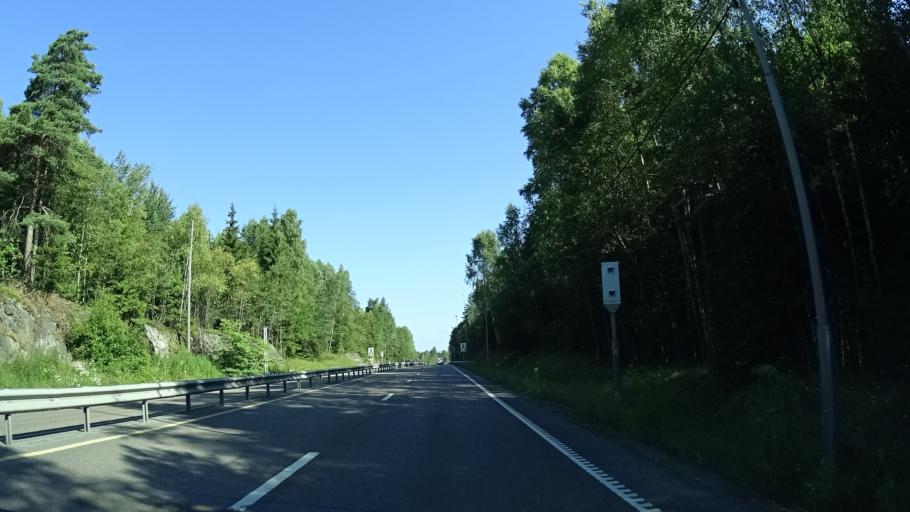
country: NO
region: Akershus
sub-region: Oppegard
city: Kolbotn
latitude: 59.7946
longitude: 10.7601
